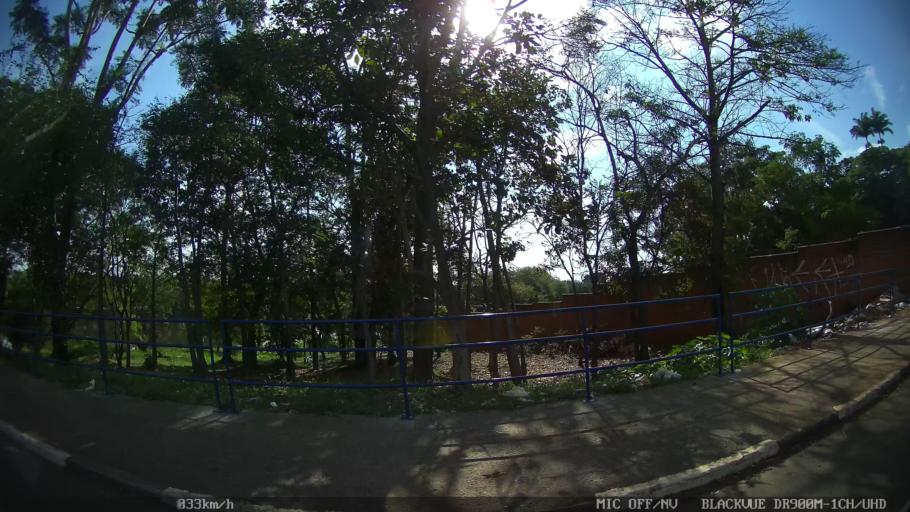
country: BR
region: Sao Paulo
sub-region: Hortolandia
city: Hortolandia
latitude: -22.8905
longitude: -47.2371
